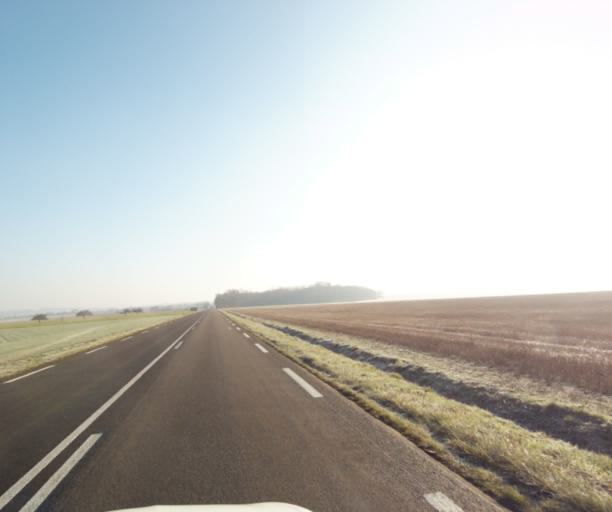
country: FR
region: Champagne-Ardenne
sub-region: Departement de la Haute-Marne
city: Montier-en-Der
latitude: 48.4309
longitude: 4.6909
